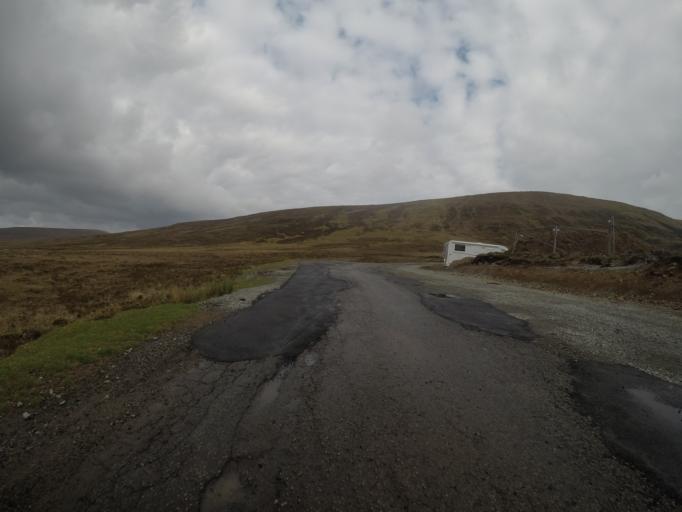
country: GB
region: Scotland
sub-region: Highland
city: Portree
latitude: 57.6271
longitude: -6.2942
